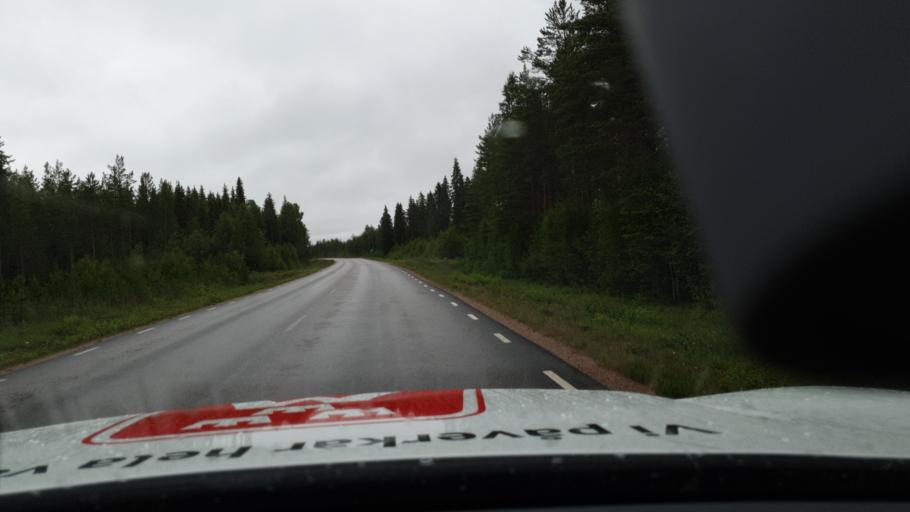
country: SE
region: Norrbotten
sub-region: Overtornea Kommun
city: OEvertornea
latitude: 66.4826
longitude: 23.6996
